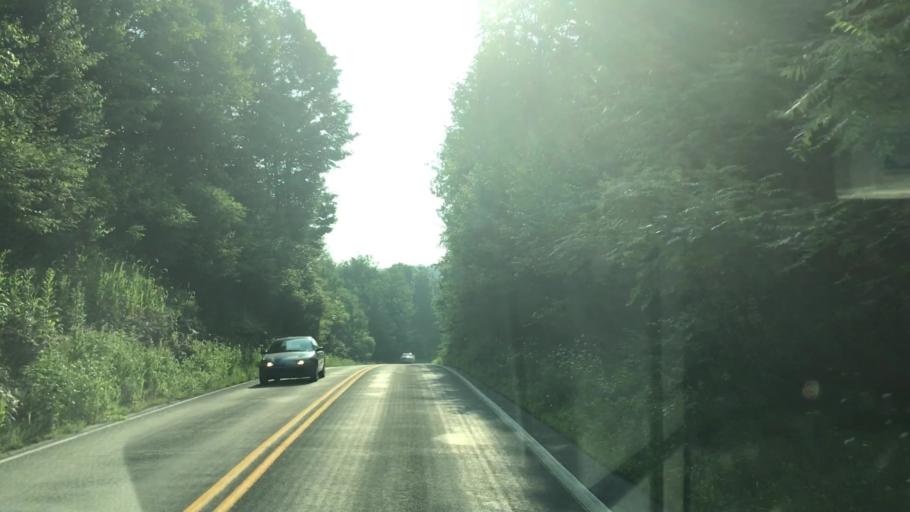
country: US
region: Pennsylvania
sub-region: Lackawanna County
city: Dalton
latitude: 41.5974
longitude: -75.6672
